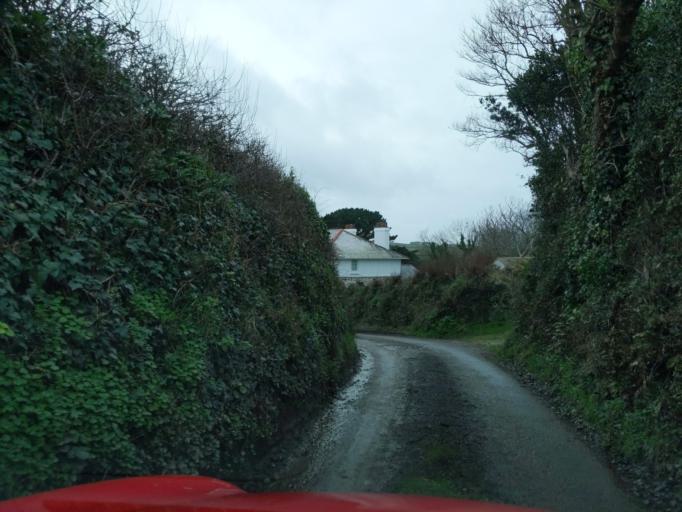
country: GB
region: England
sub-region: Cornwall
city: Fowey
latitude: 50.3393
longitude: -4.5784
